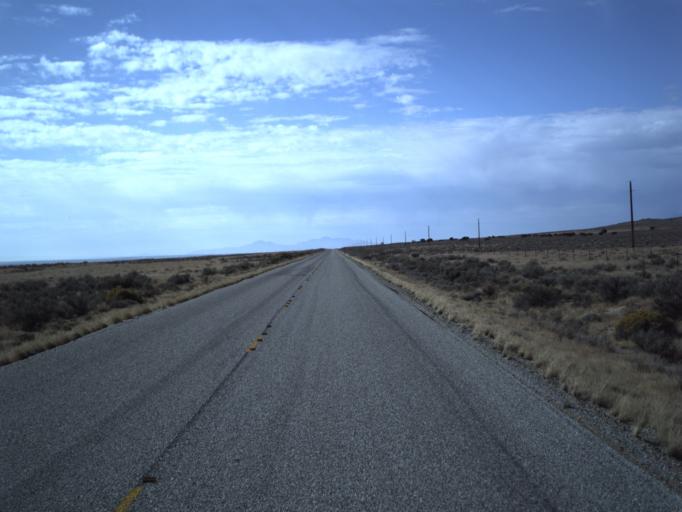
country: US
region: Utah
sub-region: Tooele County
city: Wendover
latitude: 41.5329
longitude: -113.5931
